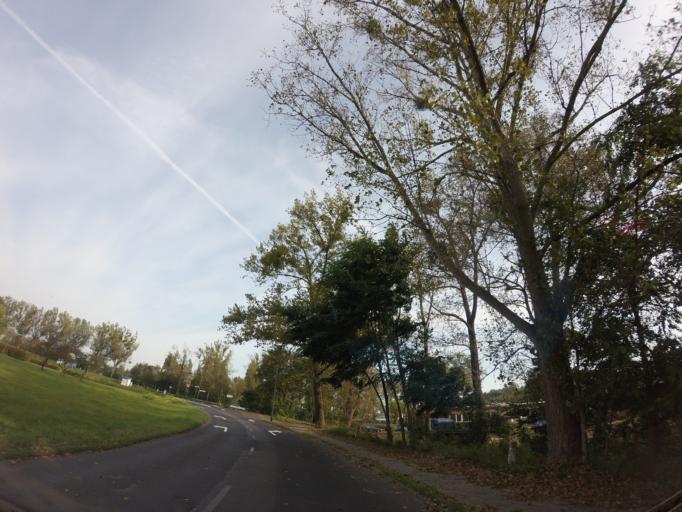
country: PL
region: West Pomeranian Voivodeship
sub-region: Szczecin
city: Szczecin
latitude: 53.3969
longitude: 14.6172
